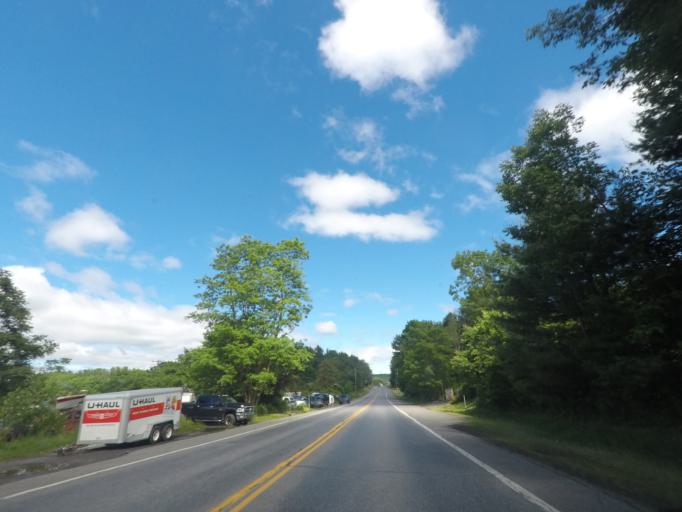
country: US
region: New York
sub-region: Columbia County
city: Philmont
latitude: 42.2093
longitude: -73.6446
